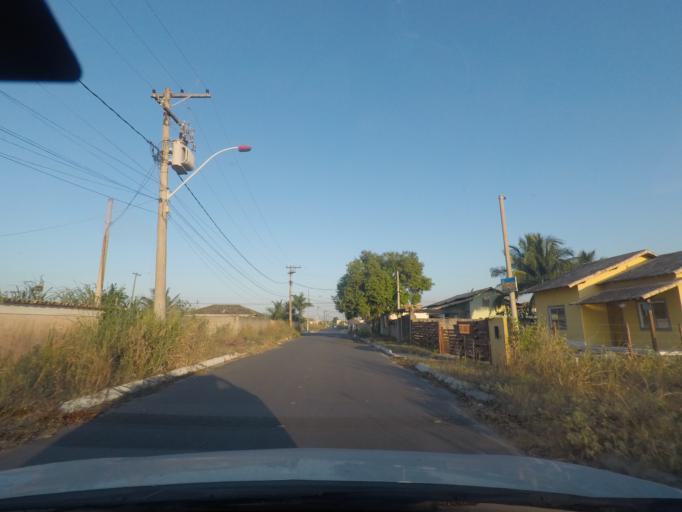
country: BR
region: Rio de Janeiro
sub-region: Marica
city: Marica
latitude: -22.9594
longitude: -42.9394
